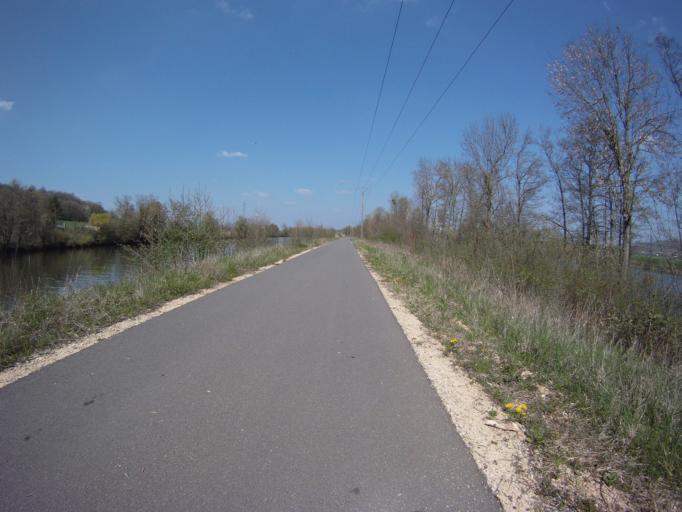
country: FR
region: Lorraine
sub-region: Departement de Meurthe-et-Moselle
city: Dieulouard
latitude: 48.8567
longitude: 6.0771
